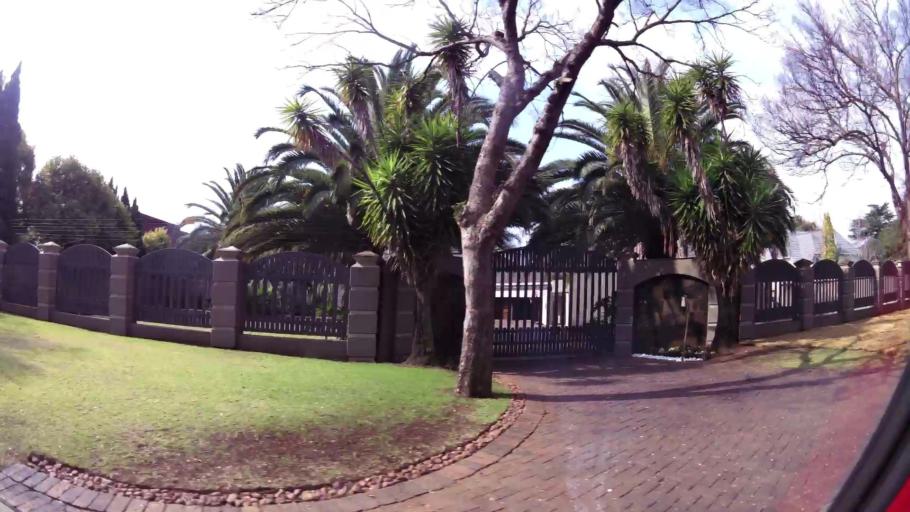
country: ZA
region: Gauteng
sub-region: Sedibeng District Municipality
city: Vanderbijlpark
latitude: -26.7380
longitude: 27.8363
